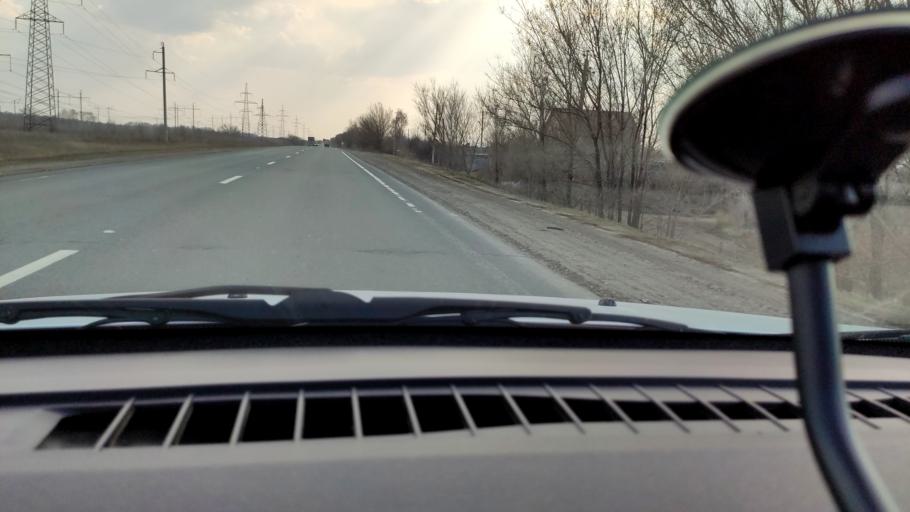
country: RU
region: Samara
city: Smyshlyayevka
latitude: 53.0870
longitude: 50.3941
